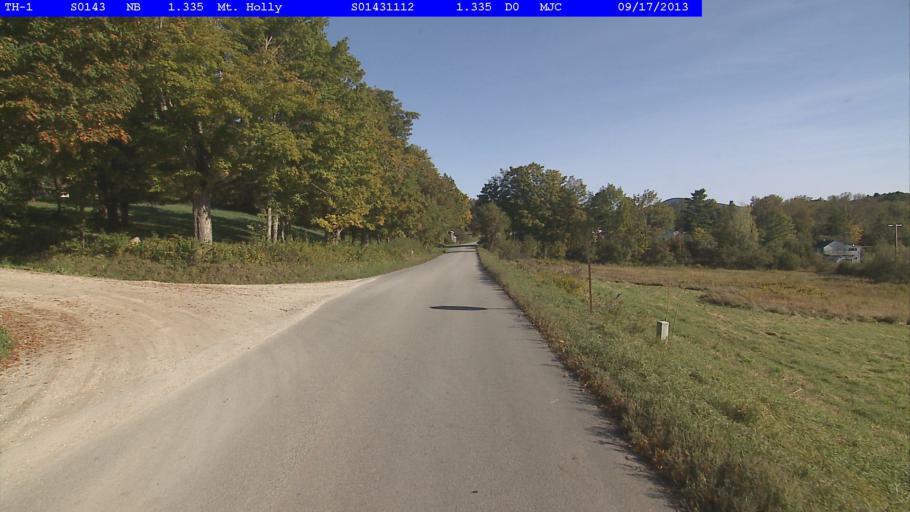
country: US
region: Vermont
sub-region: Rutland County
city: Rutland
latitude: 43.4182
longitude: -72.8209
